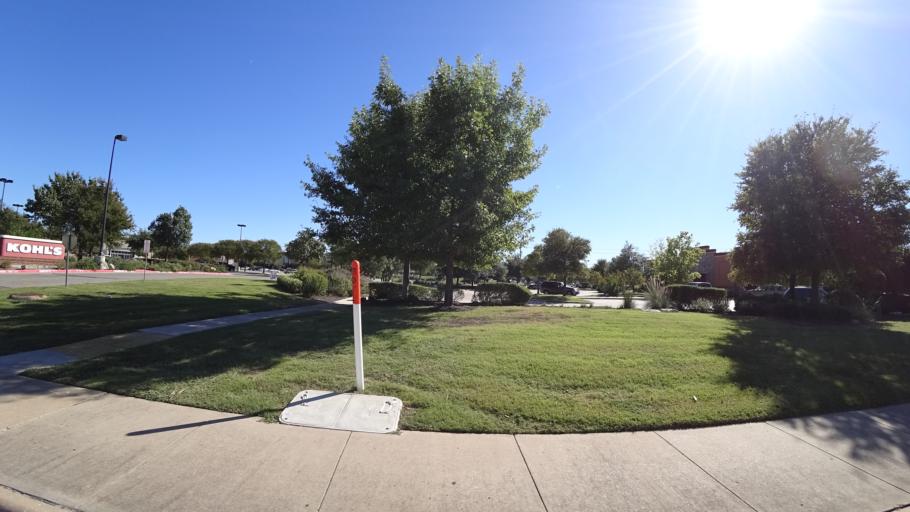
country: US
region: Texas
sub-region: Travis County
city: Rollingwood
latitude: 30.2327
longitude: -97.8162
